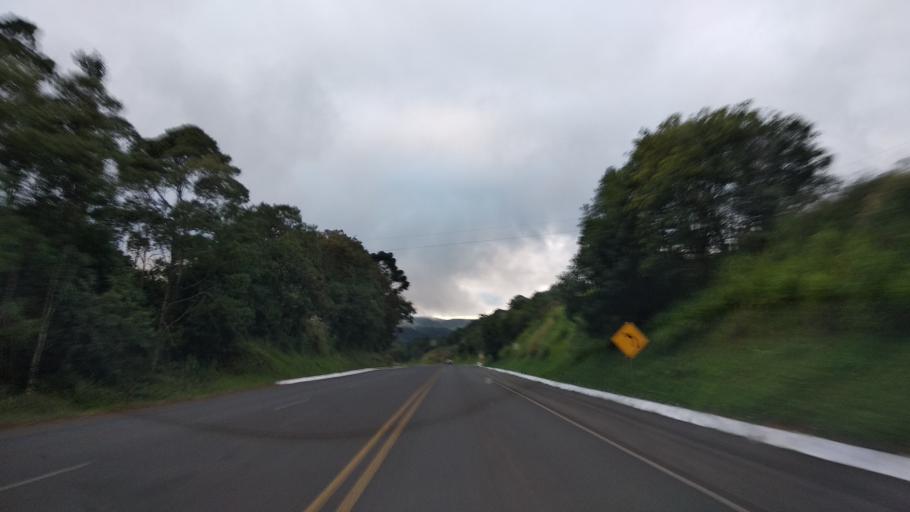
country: BR
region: Santa Catarina
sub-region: Campos Novos
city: Campos Novos
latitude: -27.4399
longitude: -51.0125
